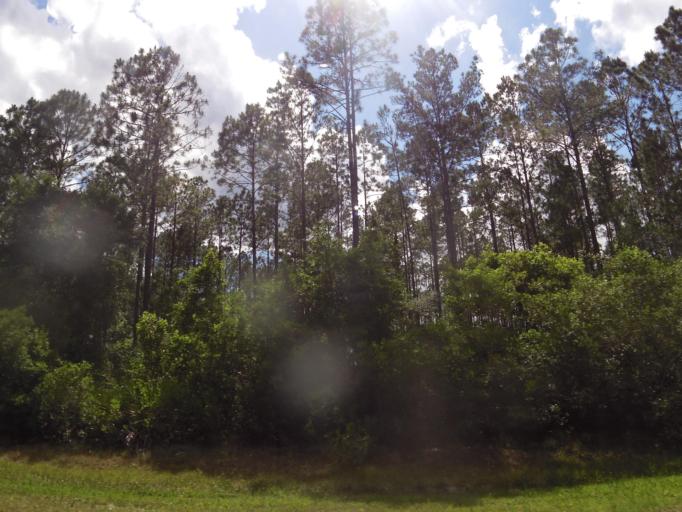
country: US
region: Florida
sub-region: Clay County
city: Asbury Lake
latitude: 29.8976
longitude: -81.8765
